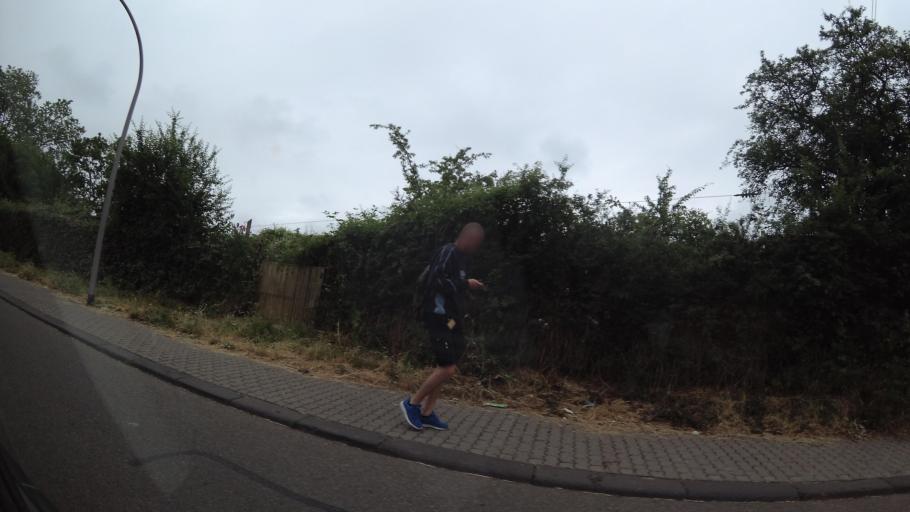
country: DE
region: Saarland
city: Saarbrucken
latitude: 49.2433
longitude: 6.9492
